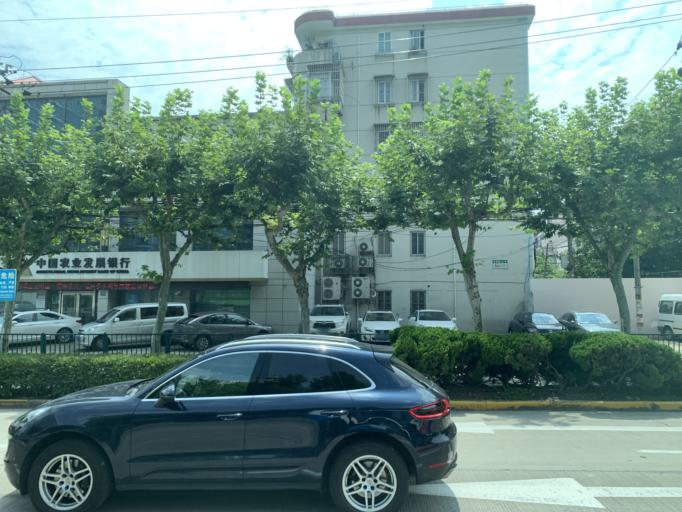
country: CN
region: Shanghai Shi
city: Pudong
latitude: 31.2389
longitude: 121.5274
